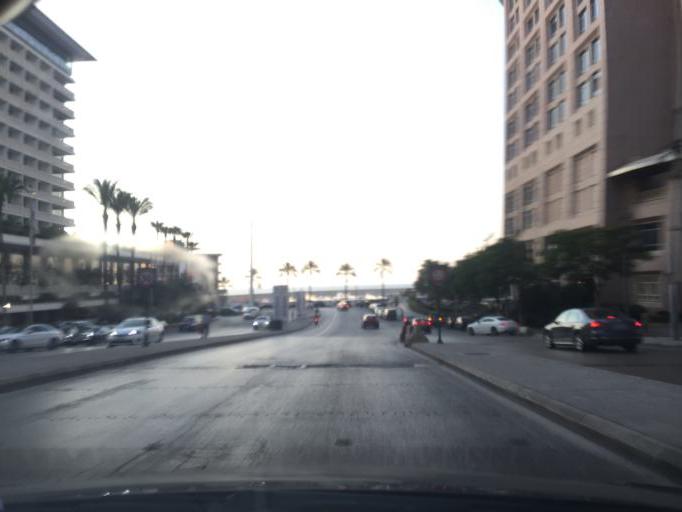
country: LB
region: Beyrouth
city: Beirut
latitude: 33.8999
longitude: 35.4956
